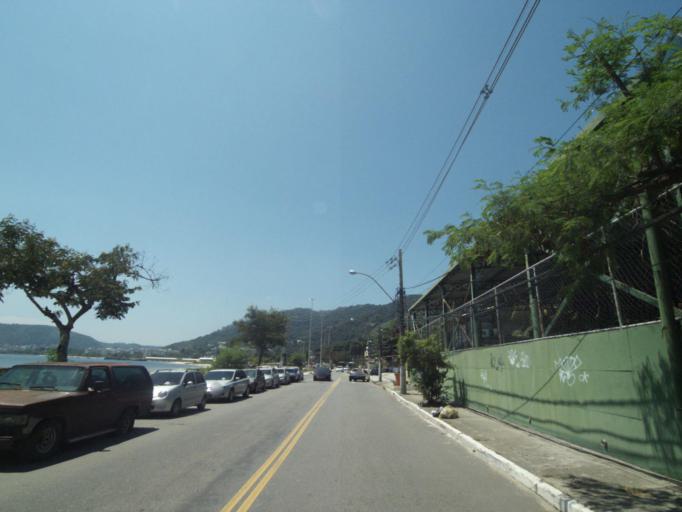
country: BR
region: Rio de Janeiro
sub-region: Niteroi
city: Niteroi
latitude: -22.9353
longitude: -43.1030
